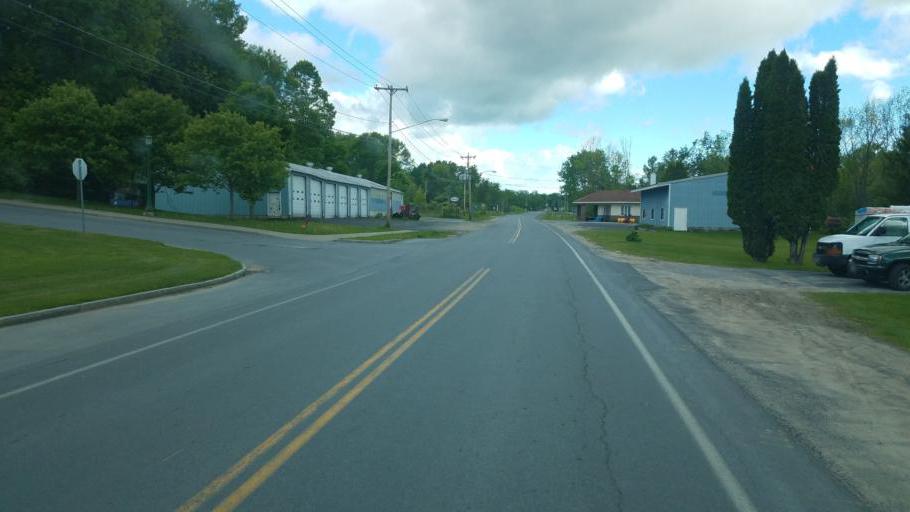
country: US
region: New York
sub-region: Oneida County
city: Boonville
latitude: 43.3329
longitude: -75.1881
